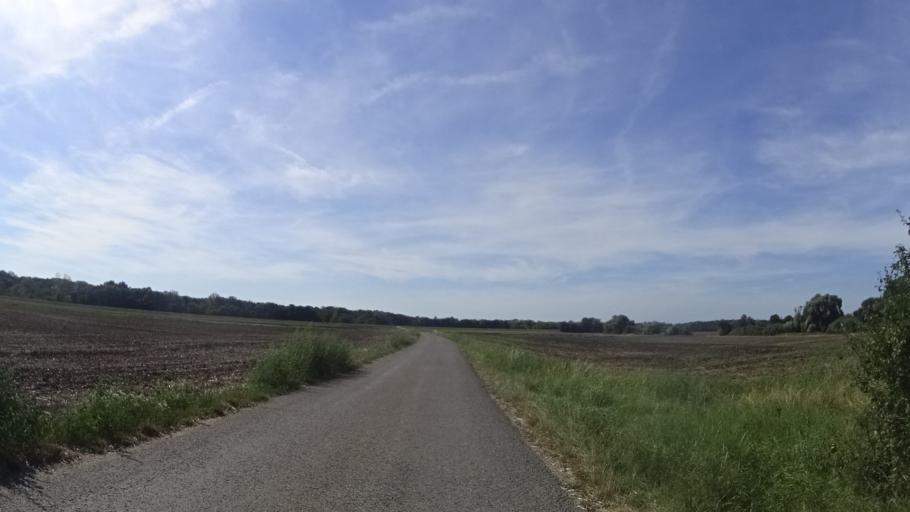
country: AT
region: Lower Austria
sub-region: Politischer Bezirk Ganserndorf
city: Durnkrut
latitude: 48.4234
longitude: 16.8683
